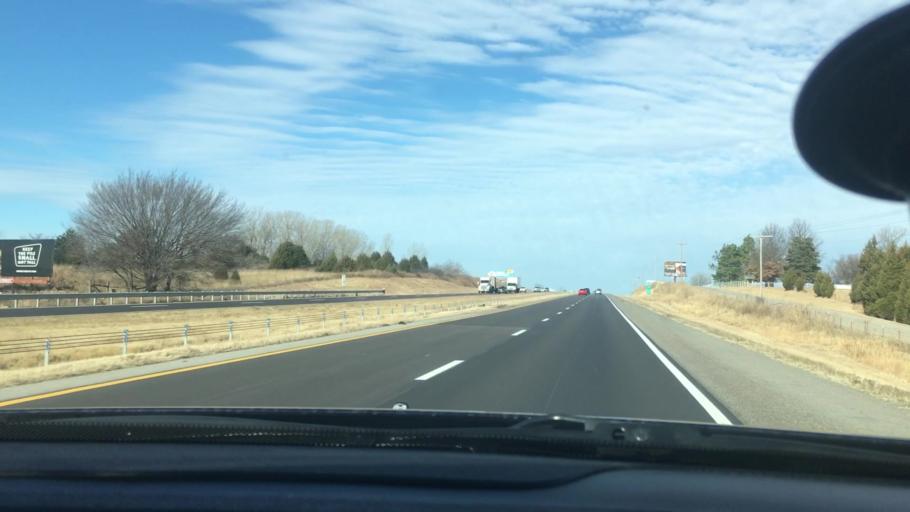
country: US
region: Oklahoma
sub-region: Cleveland County
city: Noble
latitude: 35.0884
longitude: -97.4165
